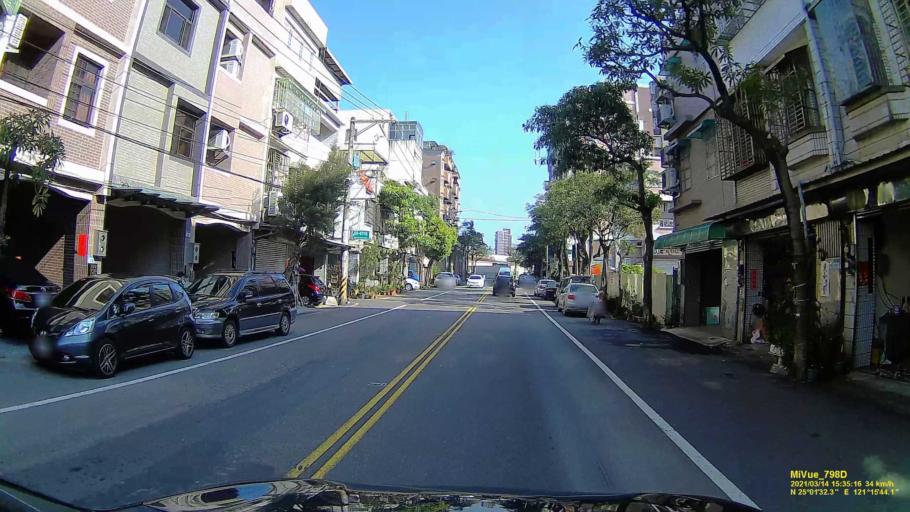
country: TW
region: Taiwan
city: Taoyuan City
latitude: 25.0255
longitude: 121.2624
